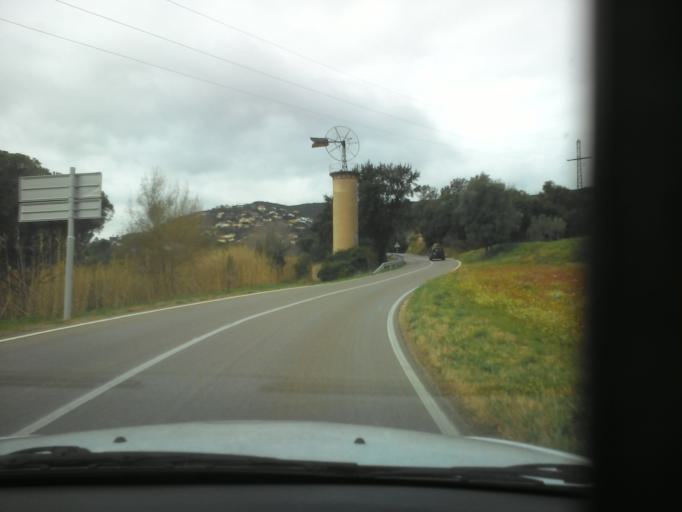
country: ES
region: Catalonia
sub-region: Provincia de Girona
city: Calonge
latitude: 41.8581
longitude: 3.0707
